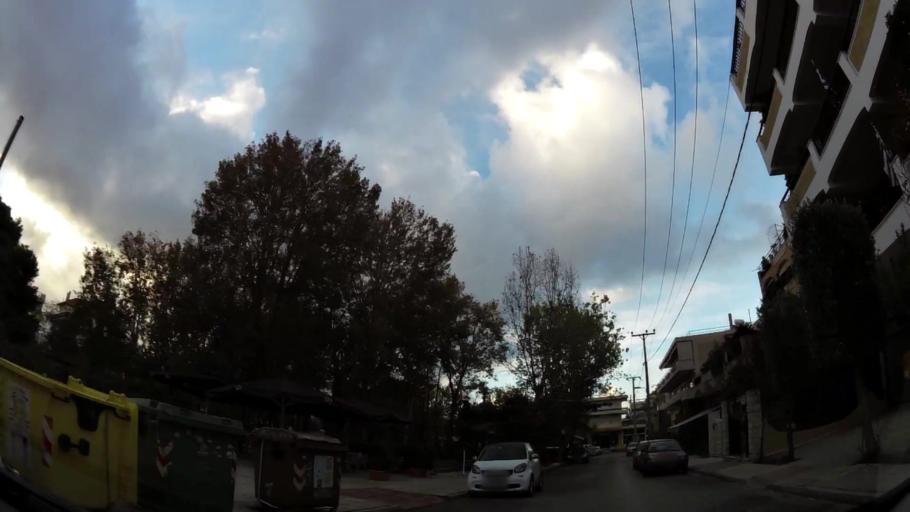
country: GR
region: Attica
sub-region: Nomarchia Athinas
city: Vrilissia
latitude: 38.0385
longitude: 23.8263
